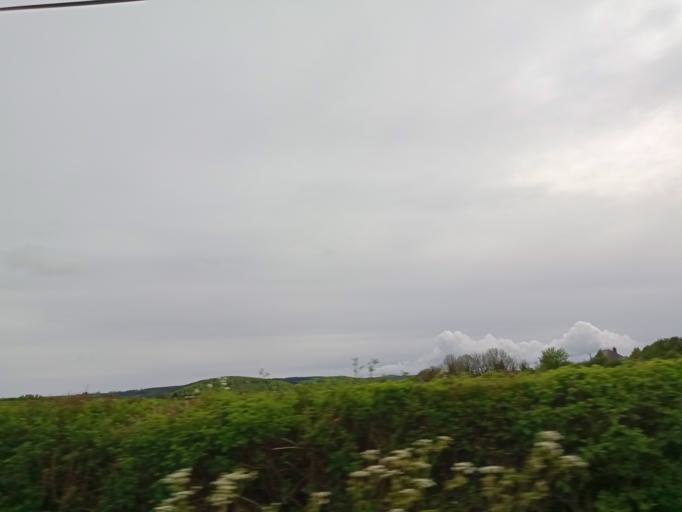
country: IE
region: Leinster
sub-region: Laois
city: Rathdowney
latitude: 52.7080
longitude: -7.4892
